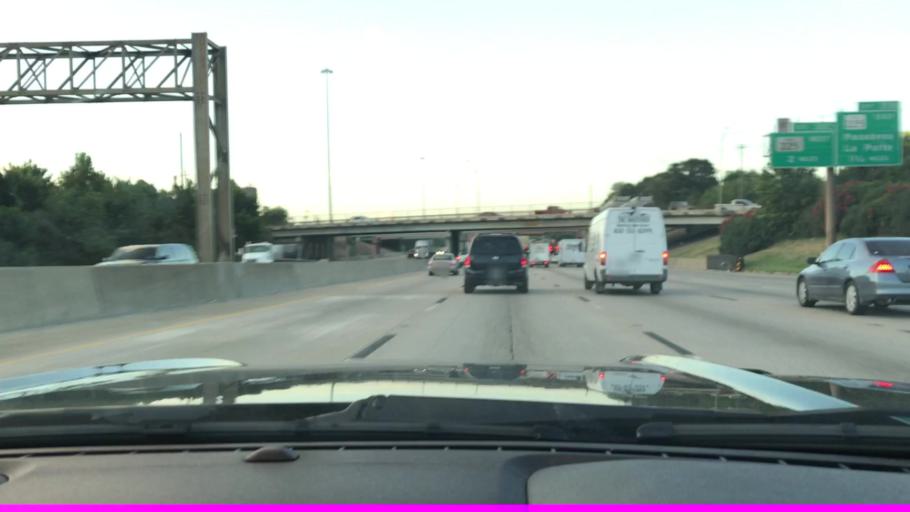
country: US
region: Texas
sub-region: Harris County
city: Galena Park
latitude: 29.7394
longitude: -95.2652
